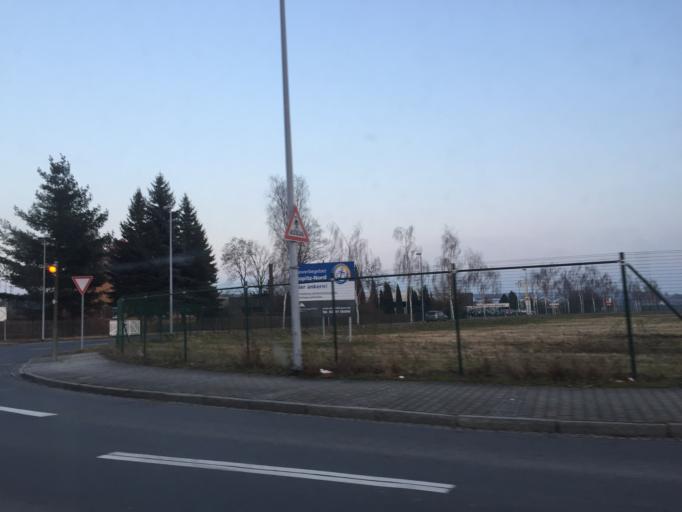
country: DE
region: Saxony
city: Pirna
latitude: 50.9796
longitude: 13.9453
